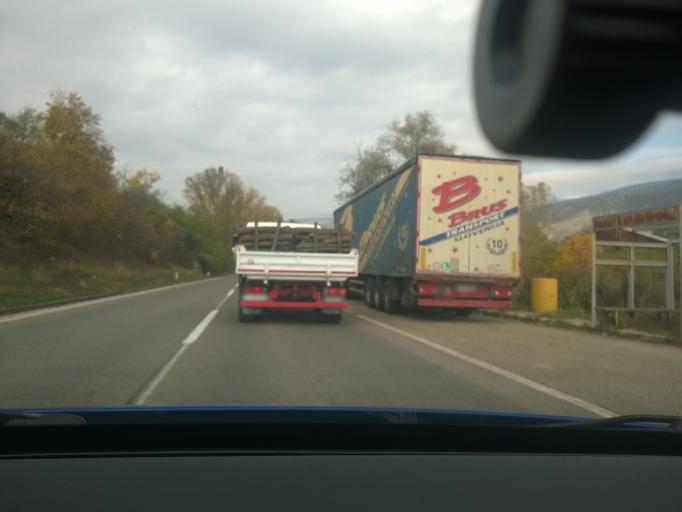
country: RS
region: Central Serbia
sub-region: Pirotski Okrug
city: Bela Palanka
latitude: 43.2789
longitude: 22.2249
